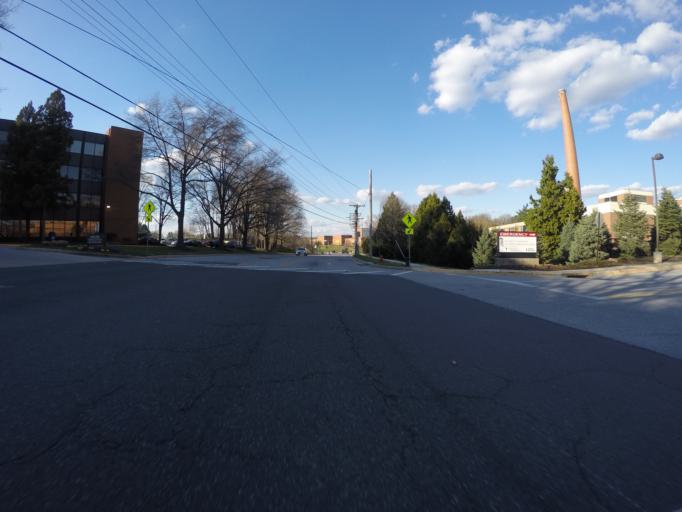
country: US
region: Maryland
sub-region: Baltimore County
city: Towson
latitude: 39.3868
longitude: -76.6127
